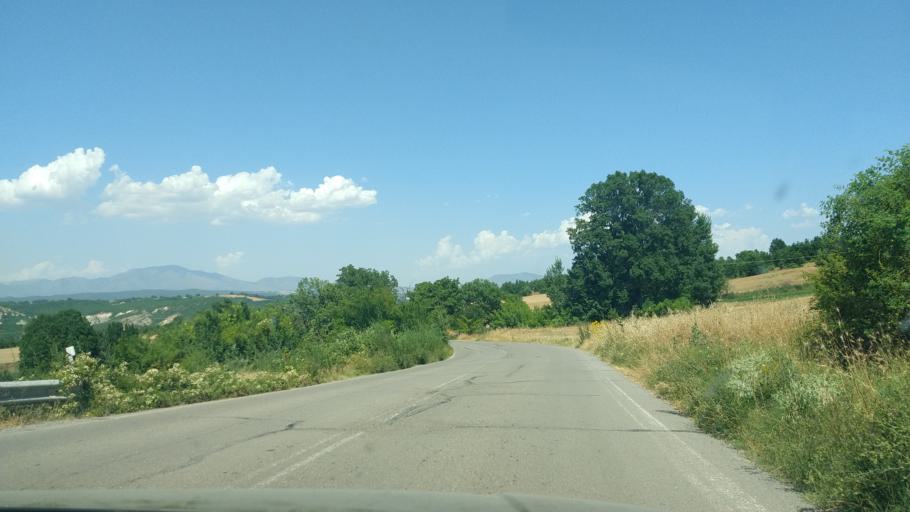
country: GR
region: West Macedonia
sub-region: Nomos Grevenon
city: Grevena
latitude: 40.0418
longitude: 21.4813
